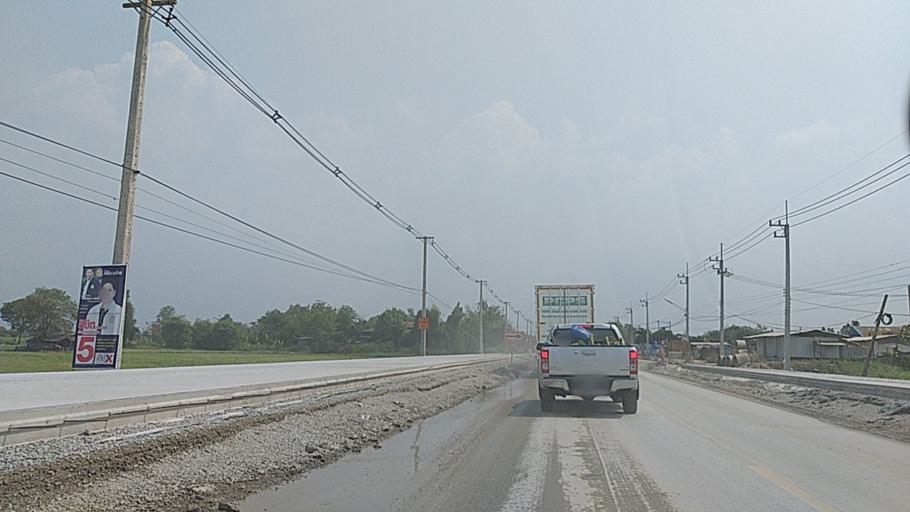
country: TH
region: Chon Buri
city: Phanat Nikhom
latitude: 13.4147
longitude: 101.1882
